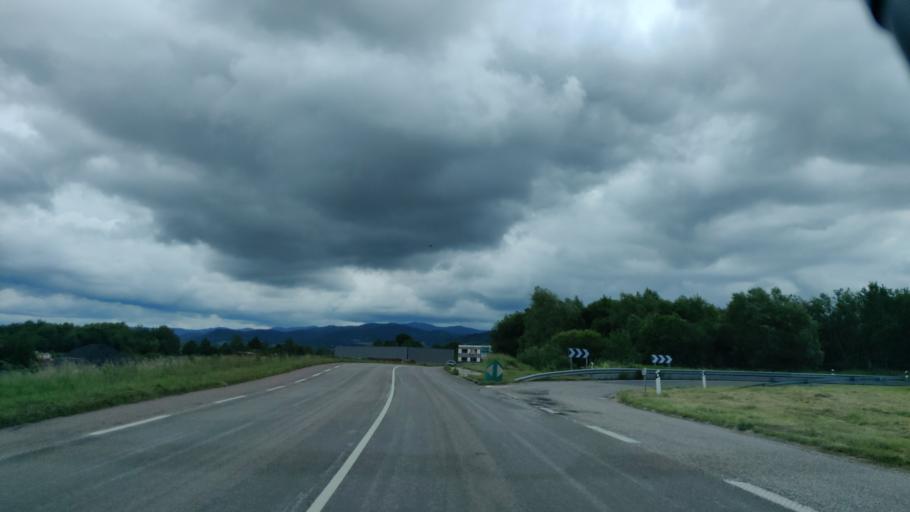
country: FR
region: Lorraine
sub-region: Departement des Vosges
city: Sainte-Marguerite
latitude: 48.2631
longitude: 6.9999
